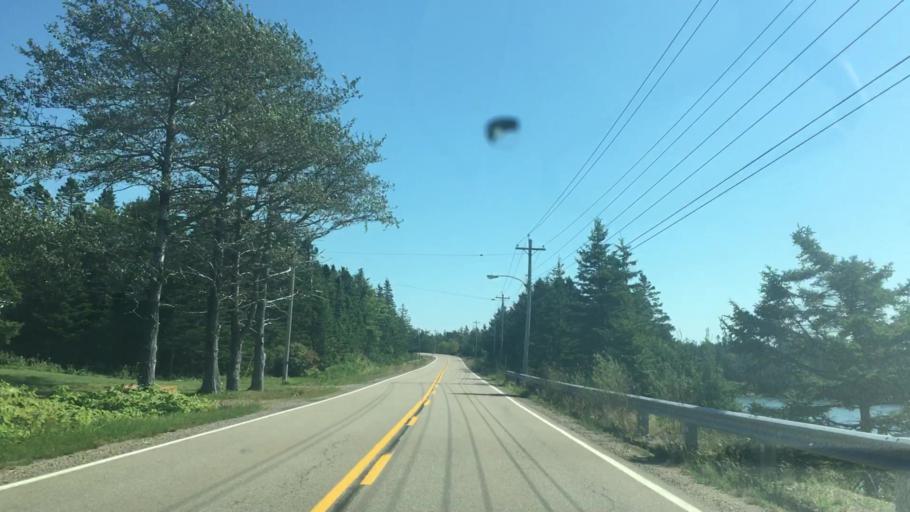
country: CA
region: Nova Scotia
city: Antigonish
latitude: 45.0219
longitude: -62.0111
